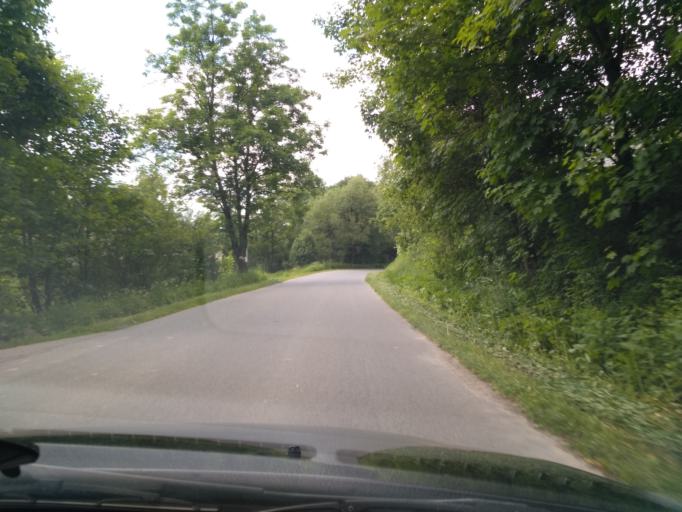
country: PL
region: Subcarpathian Voivodeship
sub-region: Powiat brzozowski
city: Wesola
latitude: 49.8056
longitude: 22.0819
